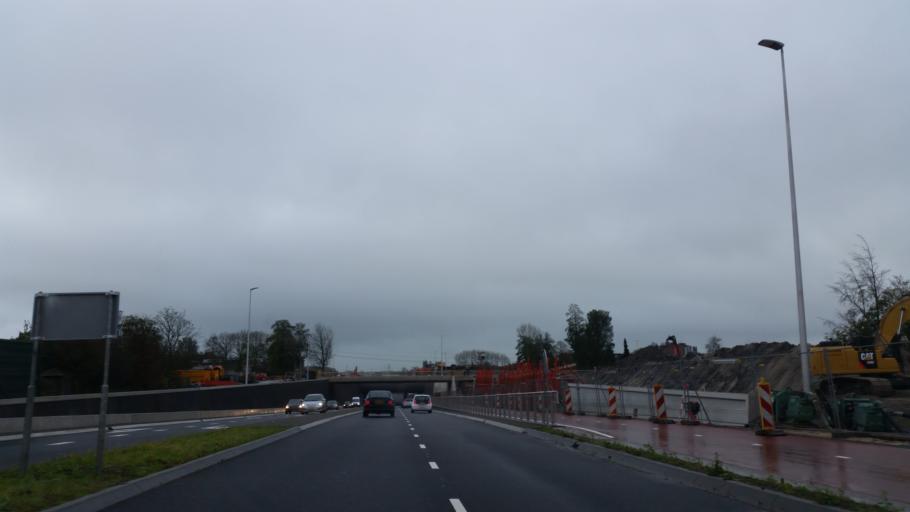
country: NL
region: Friesland
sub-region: Gemeente Leeuwarden
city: Huizum
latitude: 53.1879
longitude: 5.8177
